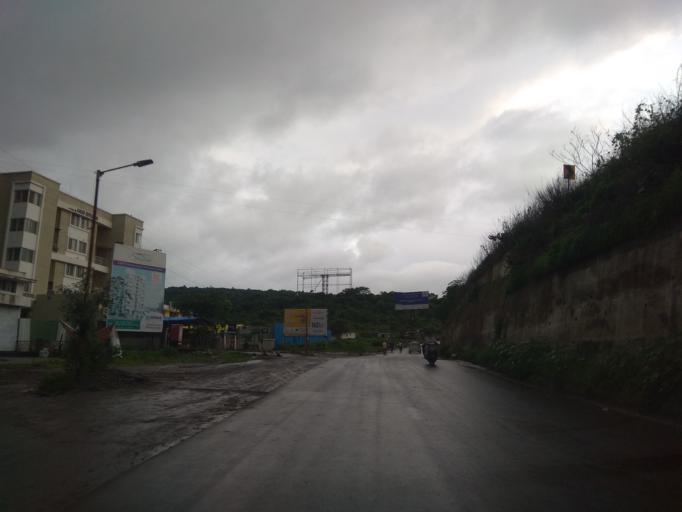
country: IN
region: Maharashtra
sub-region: Pune Division
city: Kharakvasla
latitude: 18.4932
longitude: 73.7883
